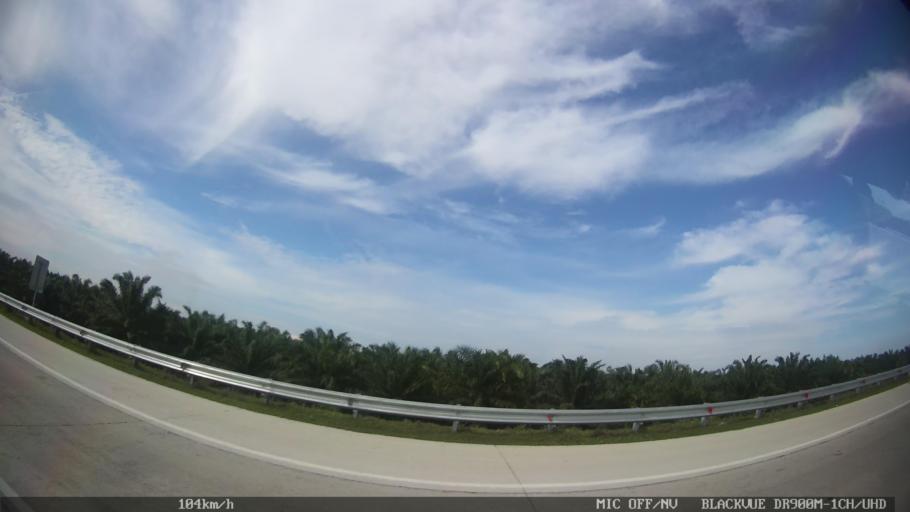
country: ID
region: North Sumatra
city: Binjai
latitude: 3.6512
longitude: 98.5384
